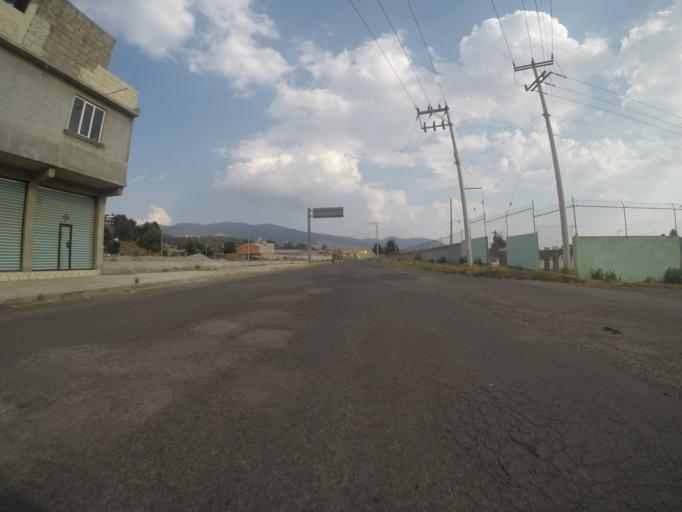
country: MX
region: Mexico
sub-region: Xalatlaco
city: El Aguila (La Mesa)
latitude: 19.1652
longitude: -99.4075
